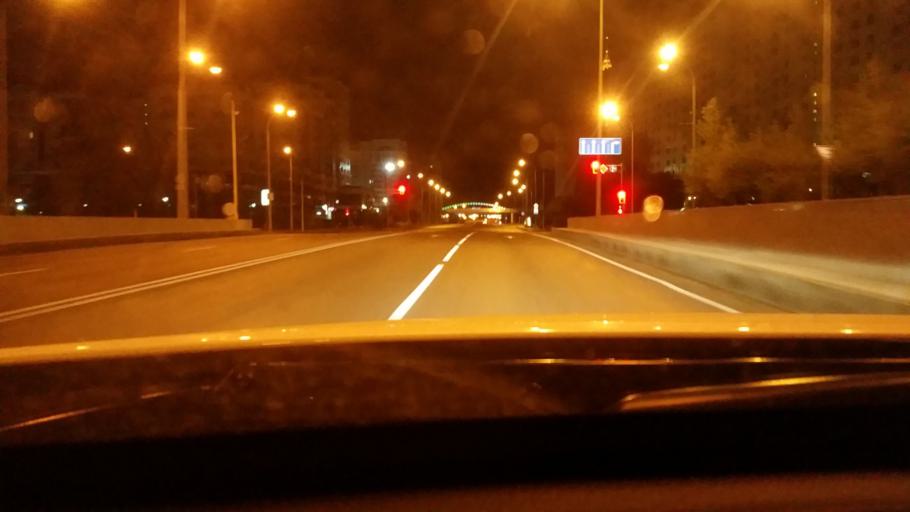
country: KZ
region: Astana Qalasy
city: Astana
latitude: 51.1238
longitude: 71.4372
